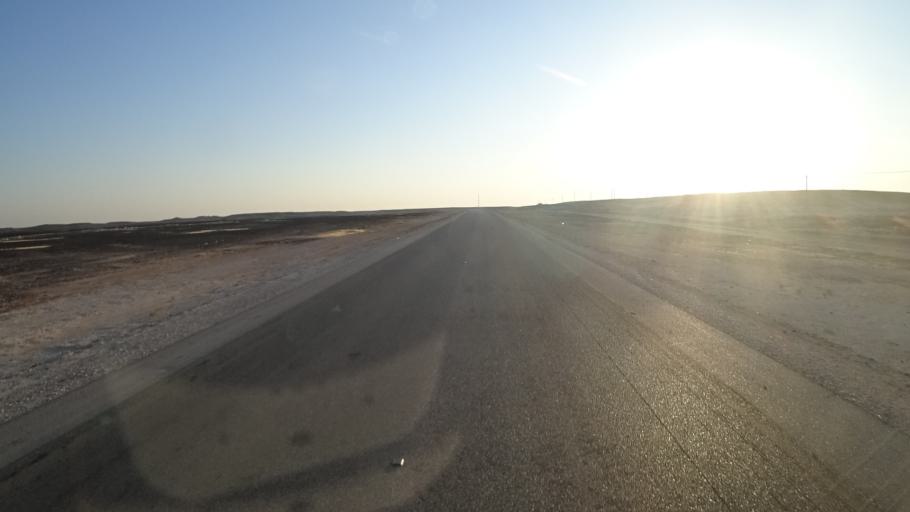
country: OM
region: Zufar
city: Salalah
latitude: 17.5496
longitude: 53.4271
